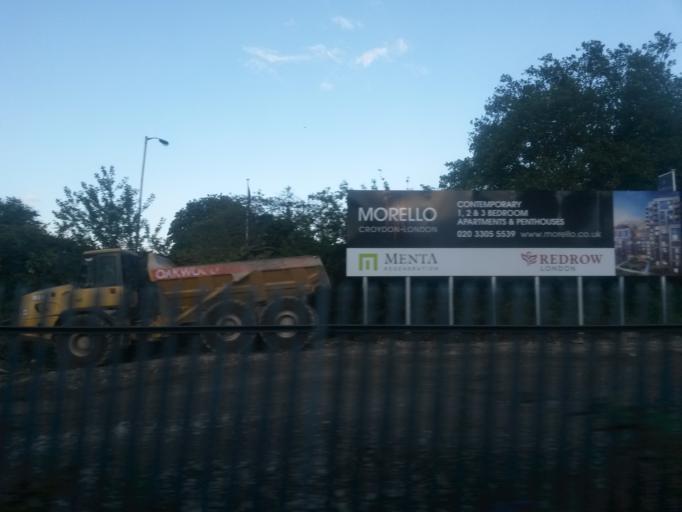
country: GB
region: England
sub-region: Greater London
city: Croydon
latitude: 51.3775
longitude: -0.0920
